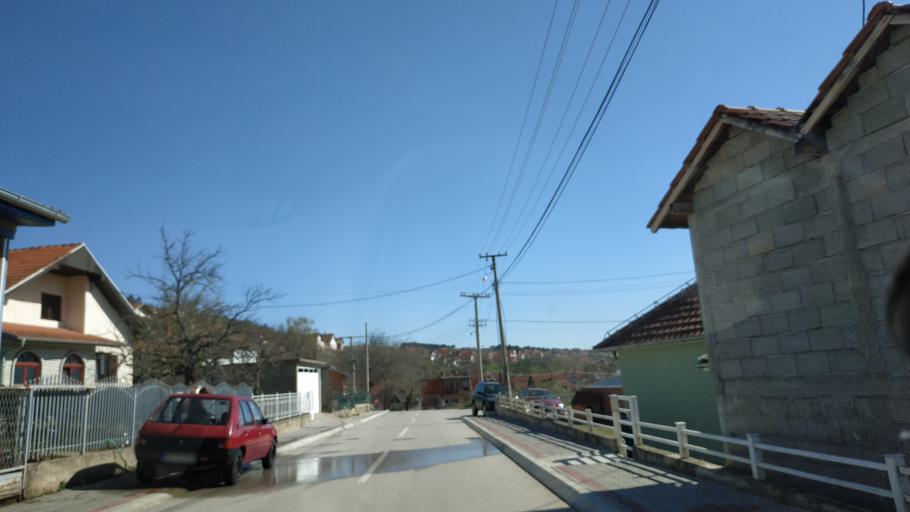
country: RS
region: Central Serbia
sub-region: Nisavski Okrug
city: Aleksinac
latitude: 43.5475
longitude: 21.7131
